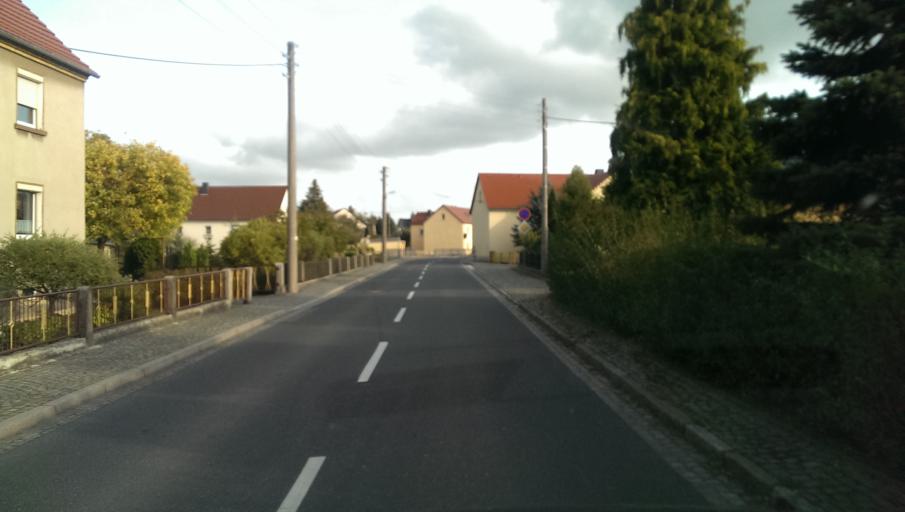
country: DE
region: Saxony
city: Haselbachtal
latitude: 51.2421
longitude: 14.0271
